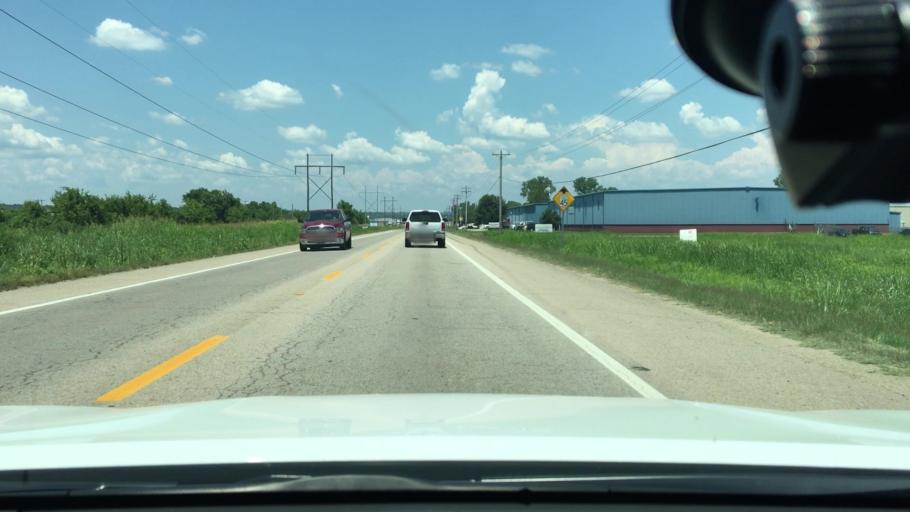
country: US
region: Arkansas
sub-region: Crawford County
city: Van Buren
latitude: 35.4081
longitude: -94.3299
